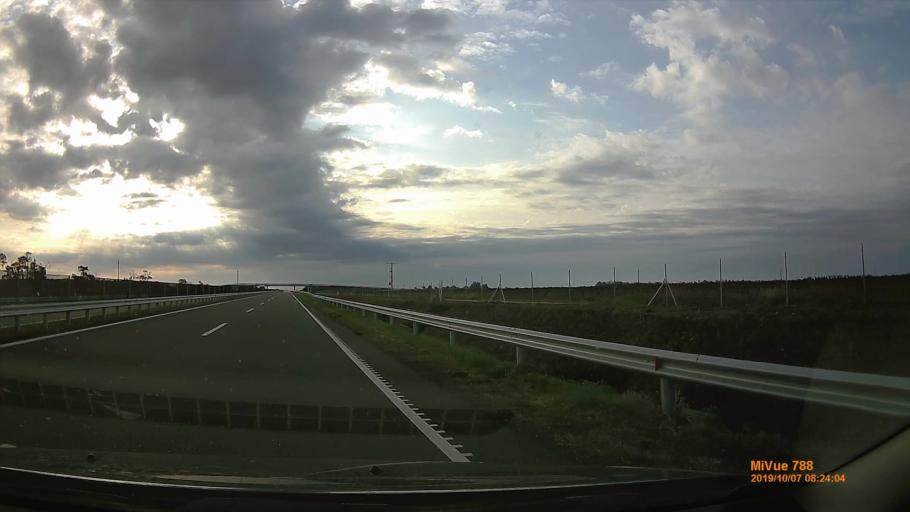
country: HU
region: Jasz-Nagykun-Szolnok
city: Kunszentmarton
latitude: 46.8417
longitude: 20.3355
